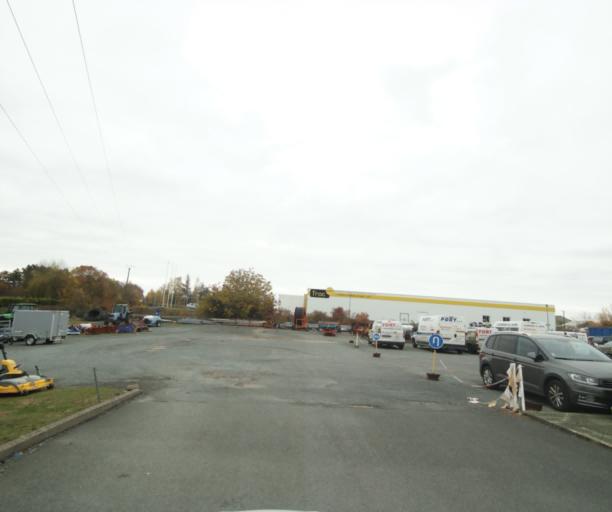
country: FR
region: Poitou-Charentes
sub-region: Departement de la Charente-Maritime
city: Les Gonds
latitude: 45.7223
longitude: -0.6395
